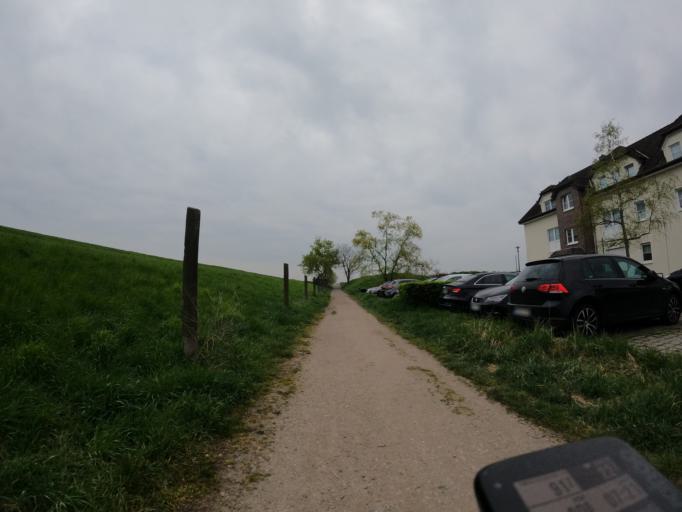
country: DE
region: Berlin
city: Gropiusstadt
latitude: 52.4100
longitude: 13.4508
